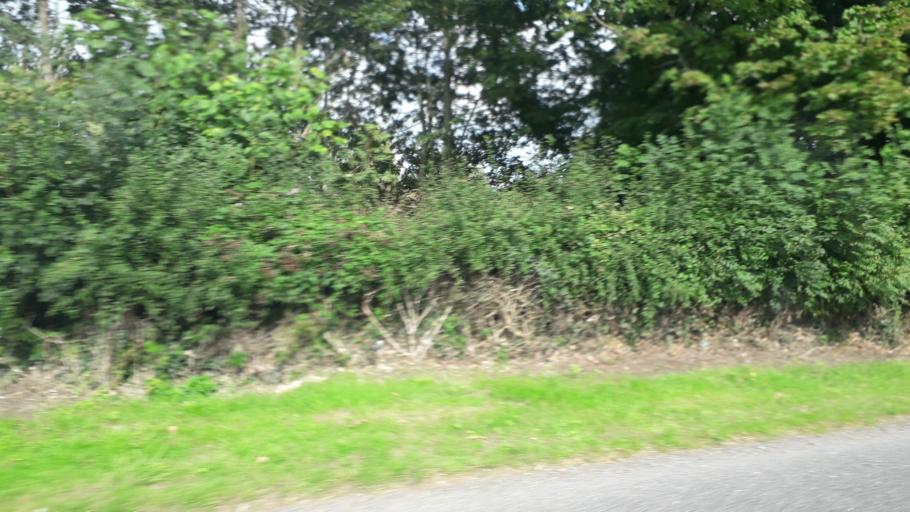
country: IE
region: Leinster
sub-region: Lu
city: Dundalk
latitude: 54.0322
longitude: -6.3584
